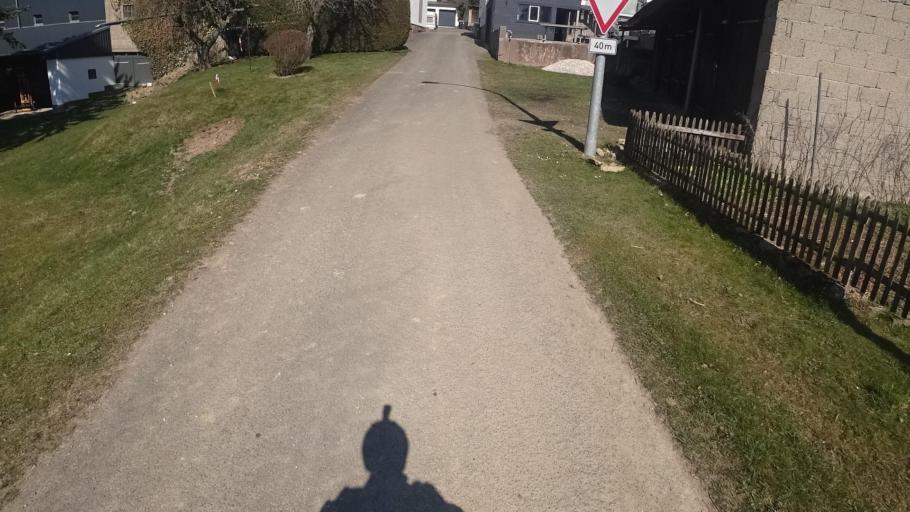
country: DE
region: Rheinland-Pfalz
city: Schnorbach
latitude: 49.9907
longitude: 7.6102
